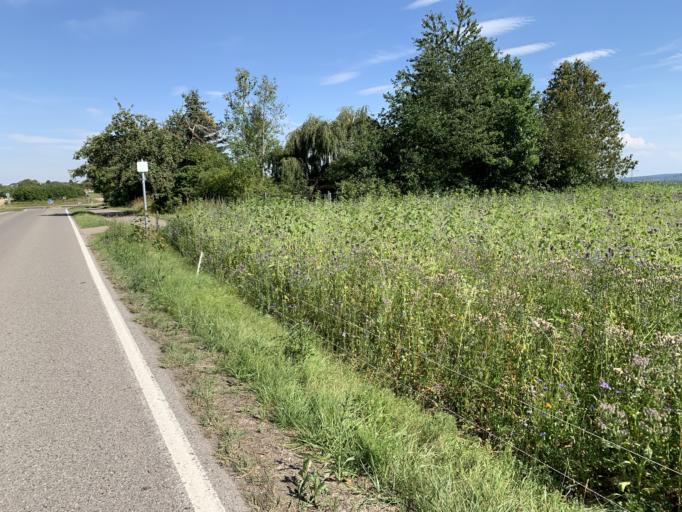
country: DE
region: Baden-Wuerttemberg
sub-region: Karlsruhe Region
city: Tiefenbronn
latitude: 48.8394
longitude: 8.8136
